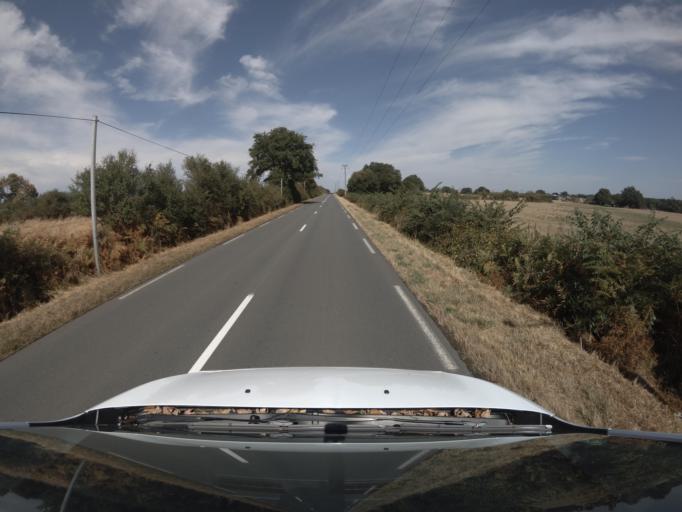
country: FR
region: Poitou-Charentes
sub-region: Departement des Deux-Sevres
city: Nueil-les-Aubiers
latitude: 46.9678
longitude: -0.5603
